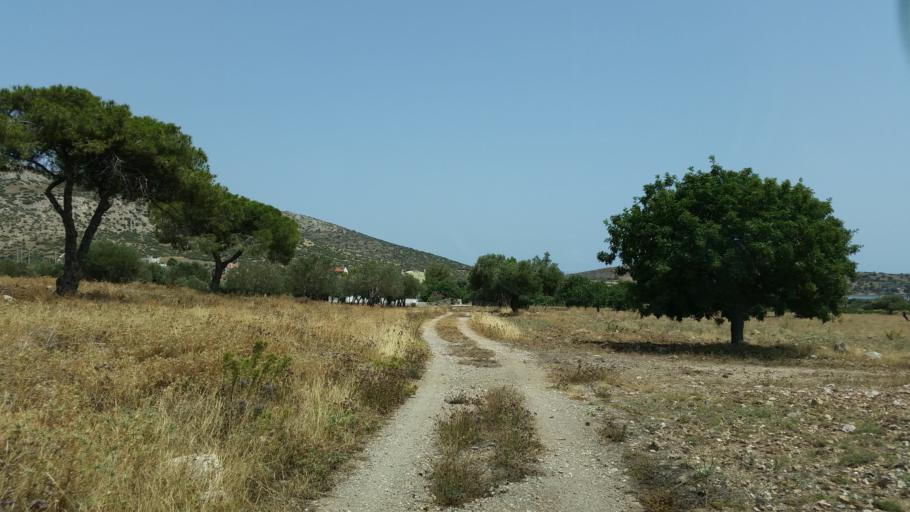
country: GR
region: Attica
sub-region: Nomarchia Anatolikis Attikis
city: Palaia Fokaia
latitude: 37.6738
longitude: 23.9649
